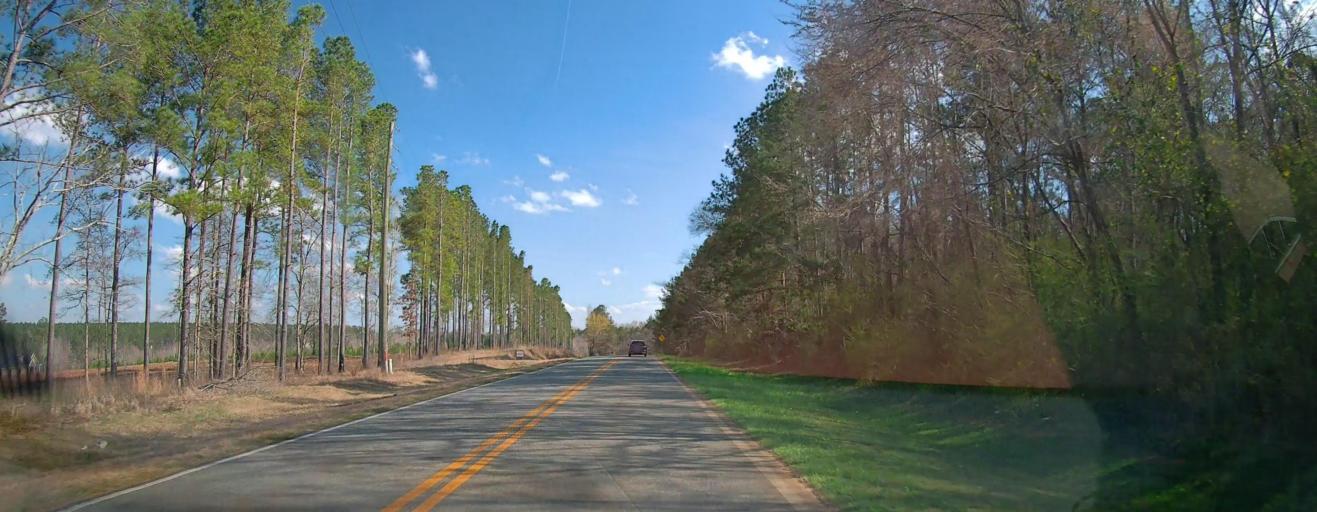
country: US
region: Georgia
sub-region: Laurens County
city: Dublin
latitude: 32.5781
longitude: -83.0500
